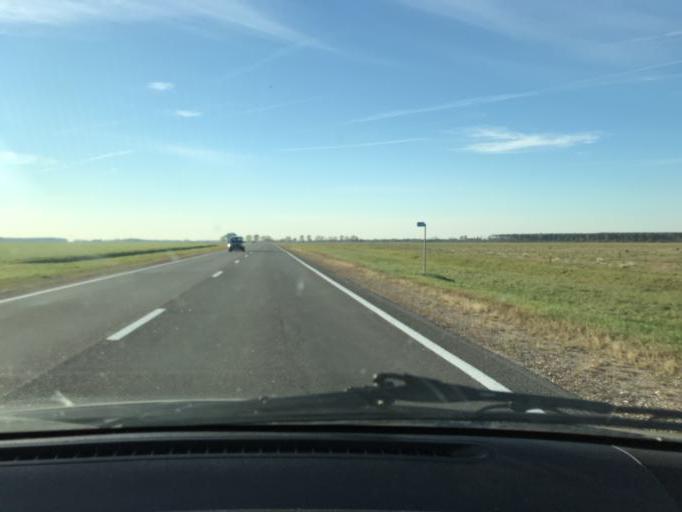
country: BY
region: Brest
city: Antopal'
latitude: 52.2259
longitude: 24.8184
